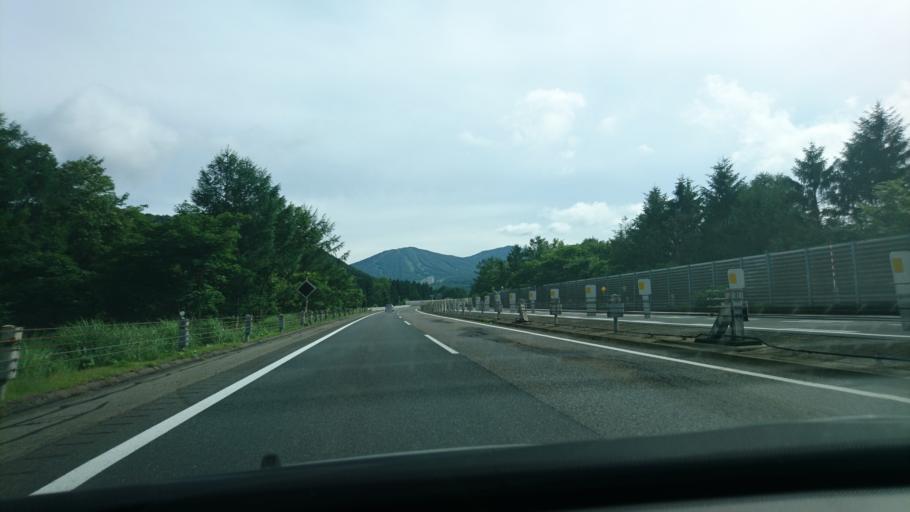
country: JP
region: Akita
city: Hanawa
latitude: 40.0381
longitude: 140.9905
